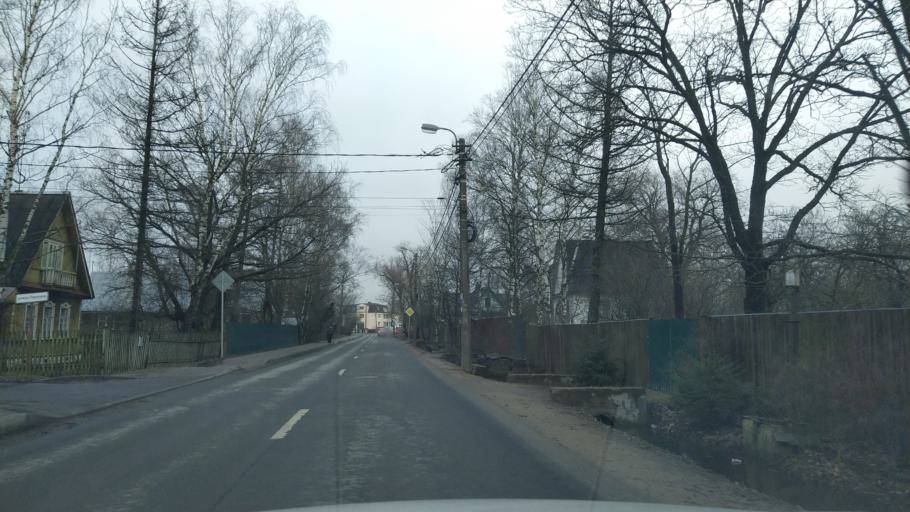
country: RU
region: St.-Petersburg
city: Aleksandrovskaya
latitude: 59.7271
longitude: 30.3534
